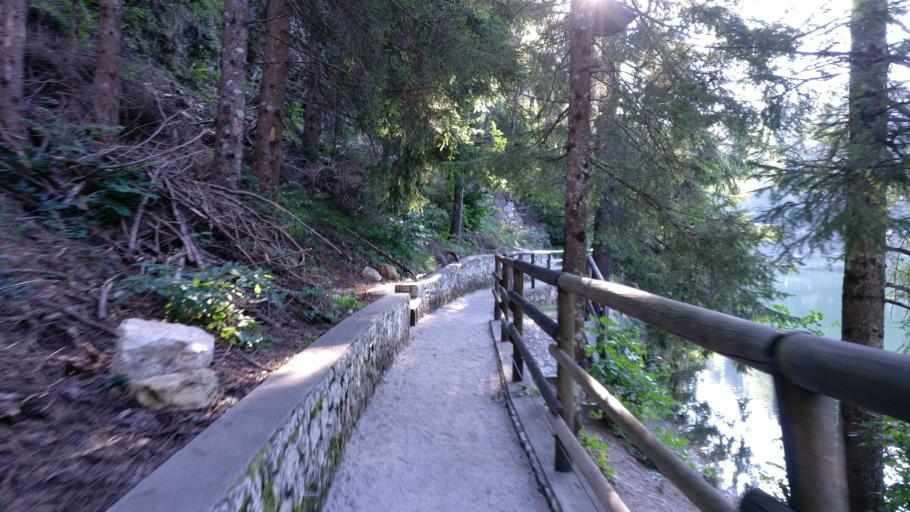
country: IT
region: Trentino-Alto Adige
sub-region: Provincia di Trento
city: Malosco
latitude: 46.4443
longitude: 11.1439
